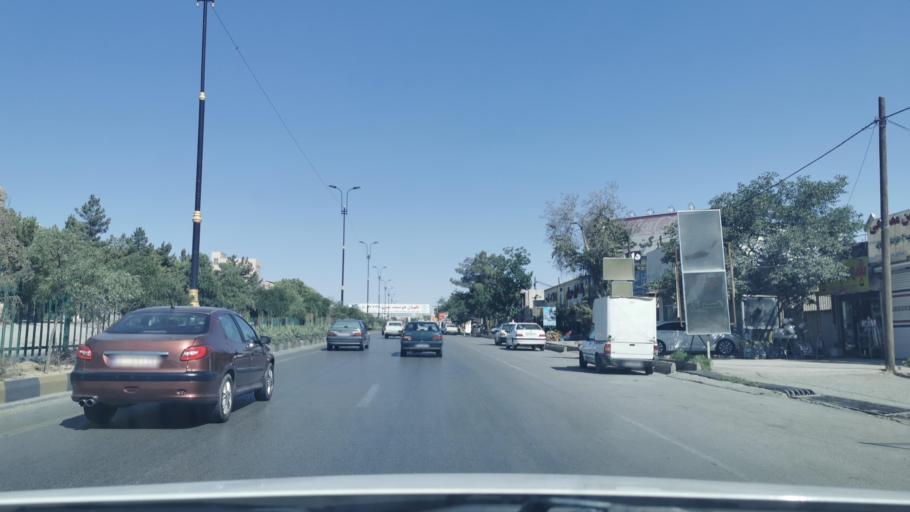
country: IR
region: Razavi Khorasan
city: Torqabeh
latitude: 36.4001
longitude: 59.3905
